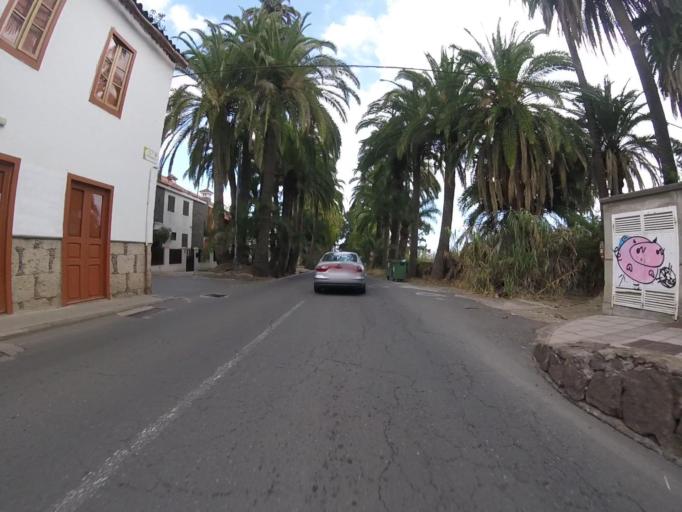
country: ES
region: Canary Islands
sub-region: Provincia de Las Palmas
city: Santa Brigida
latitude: 28.0352
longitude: -15.4964
